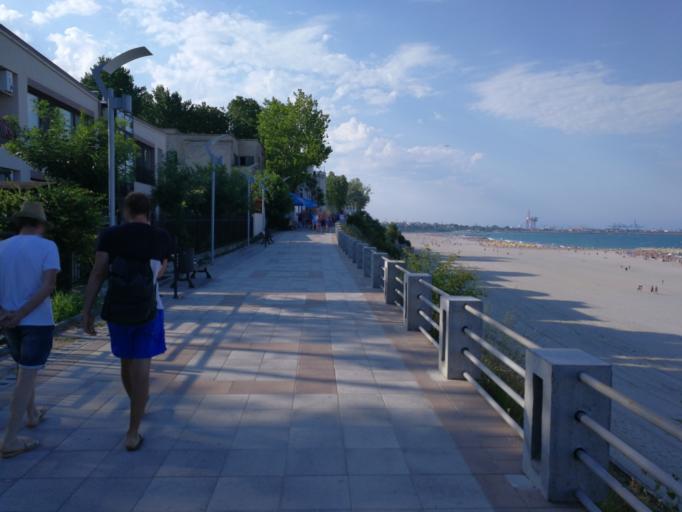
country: RO
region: Constanta
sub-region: Oras Eforie
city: Eforie Nord
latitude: 44.0648
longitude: 28.6393
